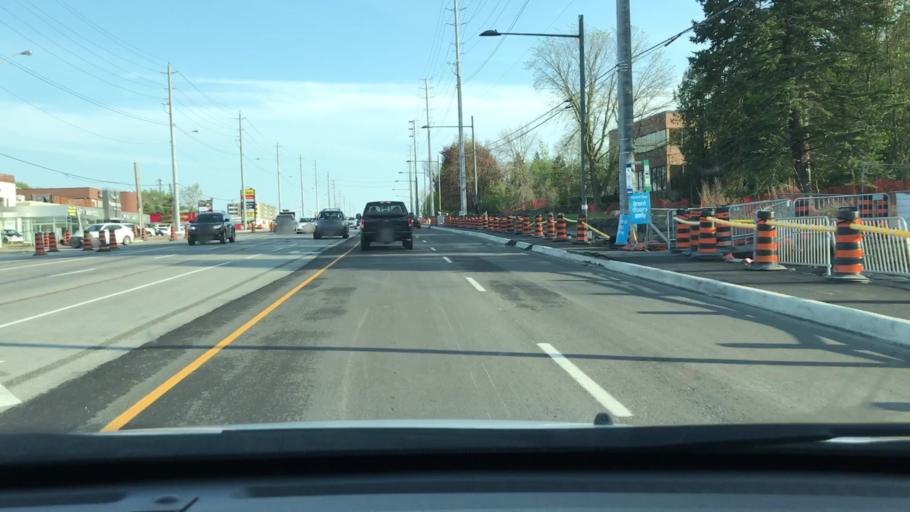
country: CA
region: Ontario
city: Newmarket
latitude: 44.0449
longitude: -79.4781
